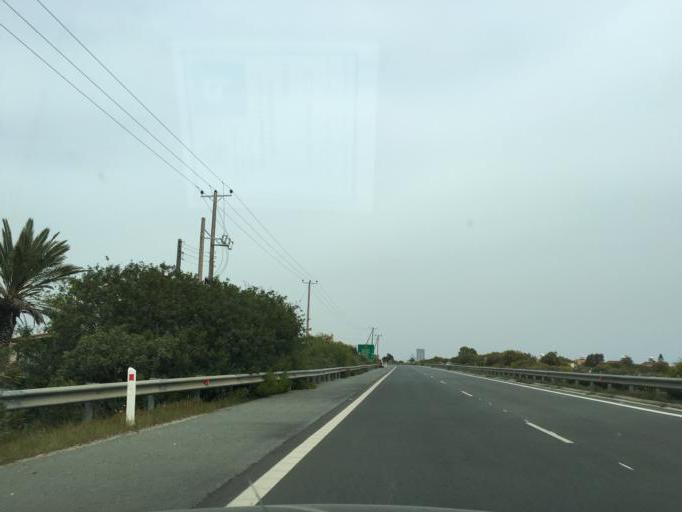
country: CY
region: Ammochostos
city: Liopetri
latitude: 34.9779
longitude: 33.9017
